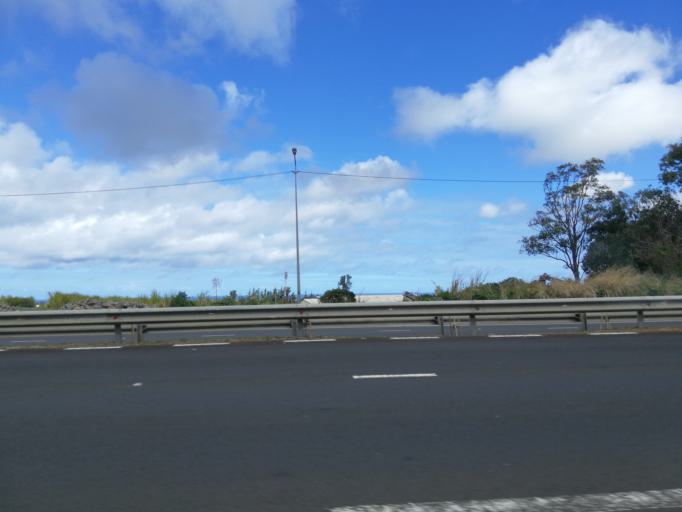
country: MU
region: Grand Port
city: Plaine Magnien
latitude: -20.4274
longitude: 57.6497
